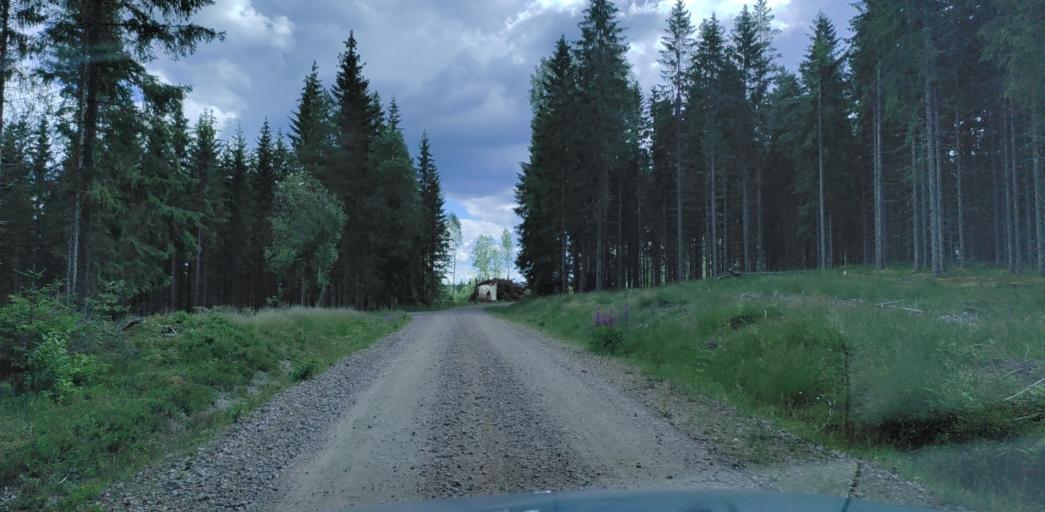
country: SE
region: Vaermland
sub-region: Hagfors Kommun
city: Ekshaerad
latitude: 60.0528
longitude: 13.3095
